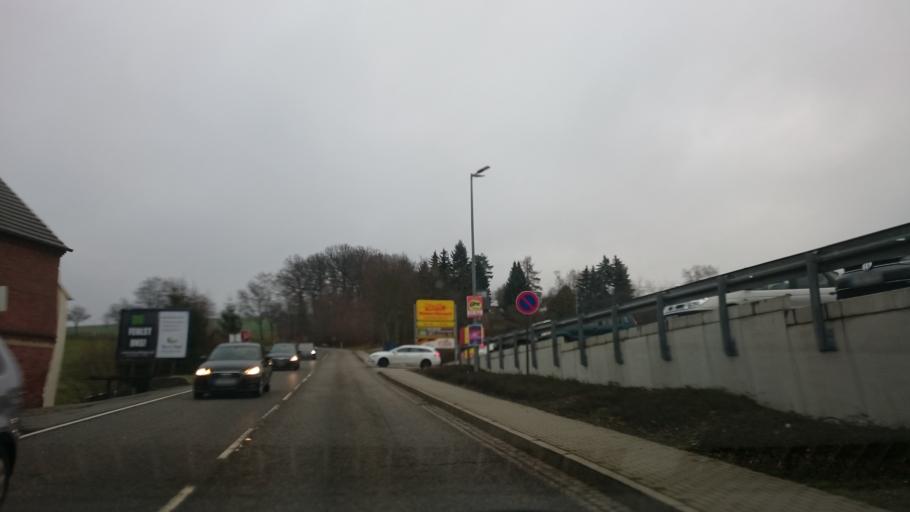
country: DE
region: Saxony
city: Mulsen
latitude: 50.7390
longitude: 12.5748
